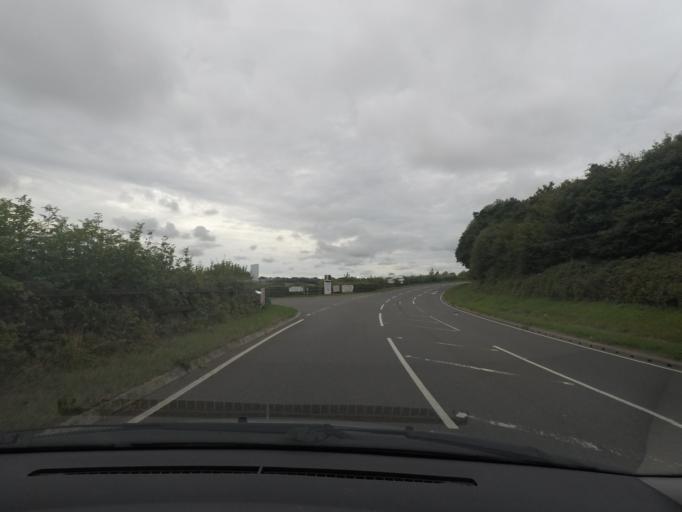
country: GB
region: England
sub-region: Wiltshire
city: Marlborough
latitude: 51.4104
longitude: -1.7350
